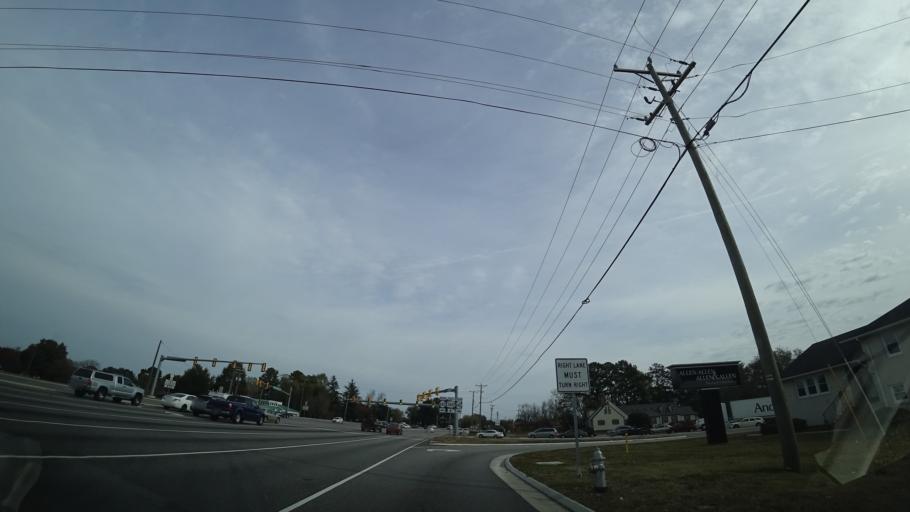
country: US
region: Virginia
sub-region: Hanover County
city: Mechanicsville
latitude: 37.6102
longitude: -77.3534
